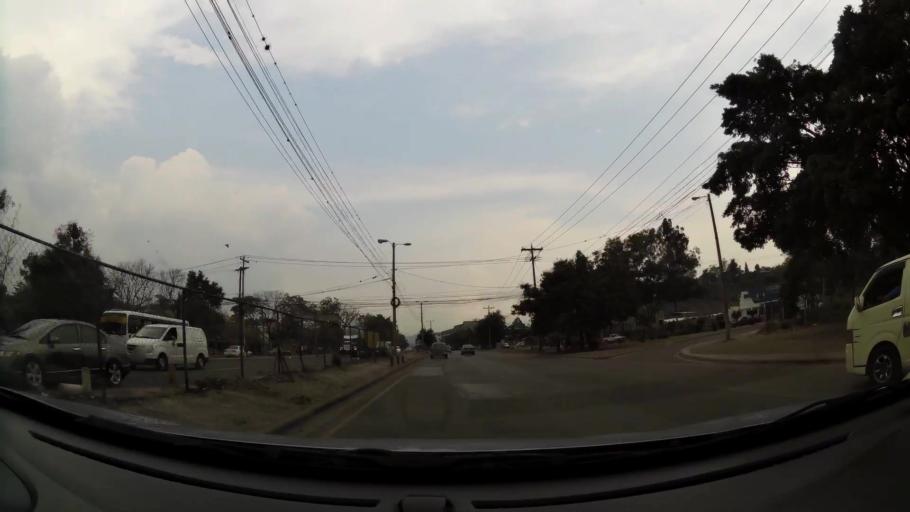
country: HN
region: Francisco Morazan
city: Tegucigalpa
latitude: 14.0801
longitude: -87.2170
